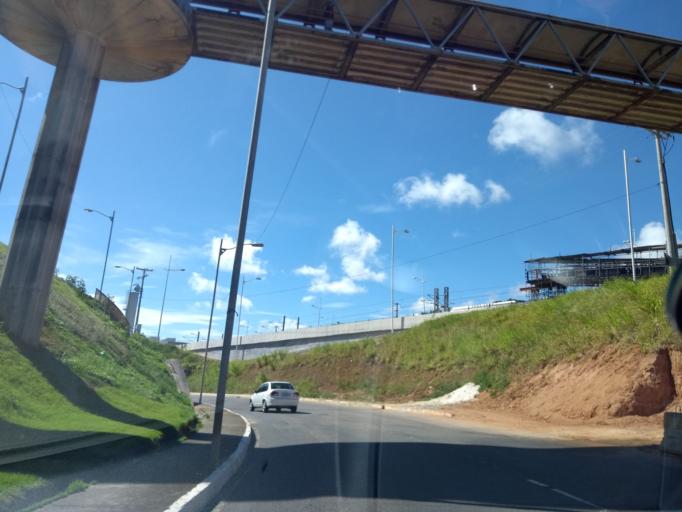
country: BR
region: Bahia
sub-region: Salvador
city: Salvador
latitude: -12.9765
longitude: -38.4553
